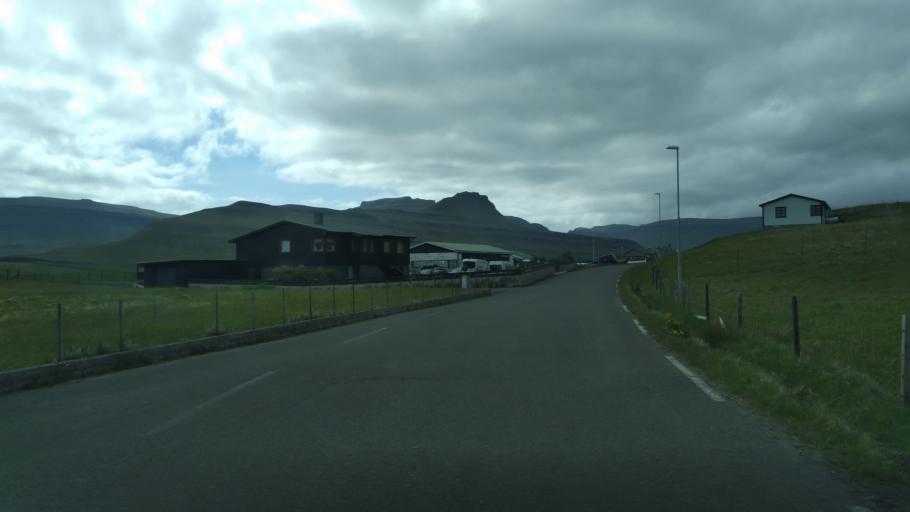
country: FO
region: Suduroy
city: Tvoroyri
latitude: 61.5457
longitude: -6.7820
